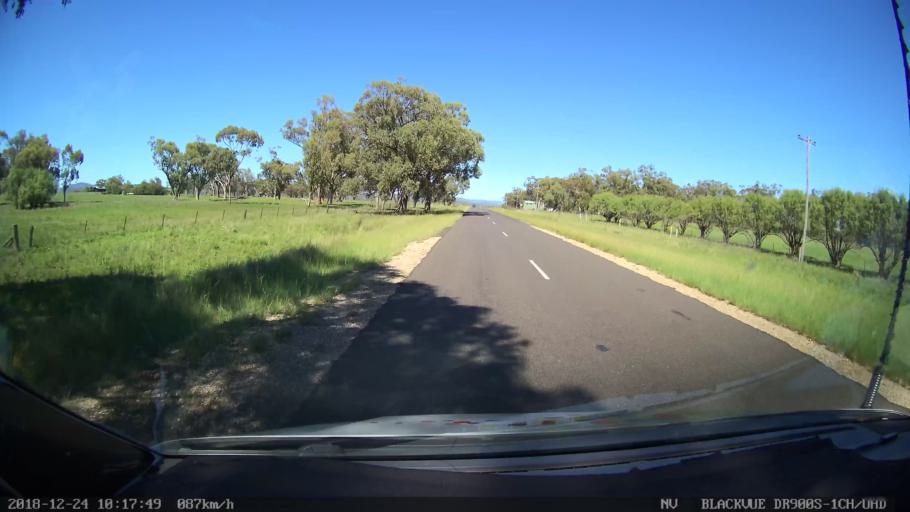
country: AU
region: New South Wales
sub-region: Liverpool Plains
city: Quirindi
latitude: -31.7214
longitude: 150.5858
